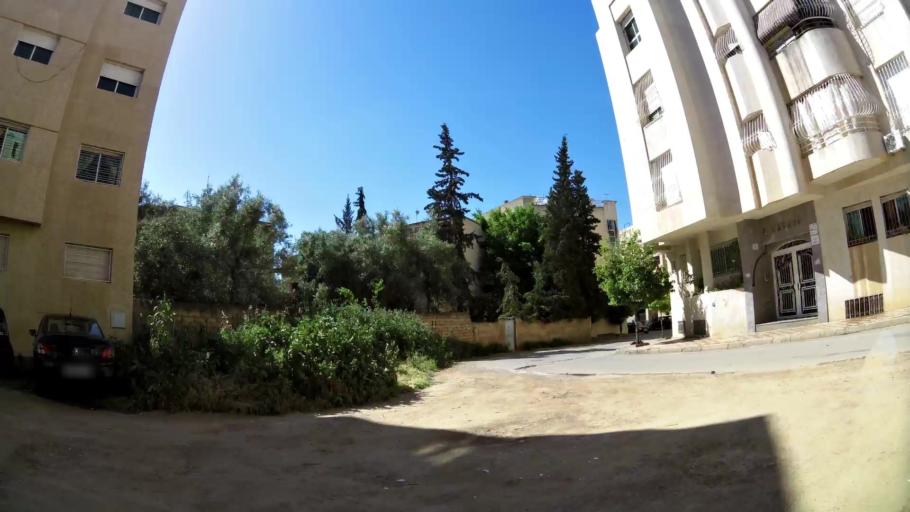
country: MA
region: Fes-Boulemane
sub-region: Fes
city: Fes
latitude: 34.0257
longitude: -4.9930
